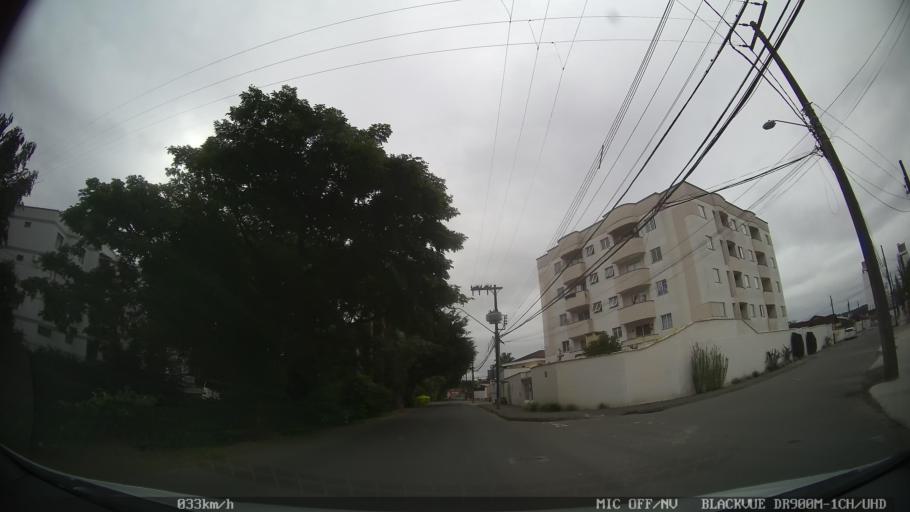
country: BR
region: Santa Catarina
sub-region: Joinville
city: Joinville
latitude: -26.2708
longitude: -48.8692
